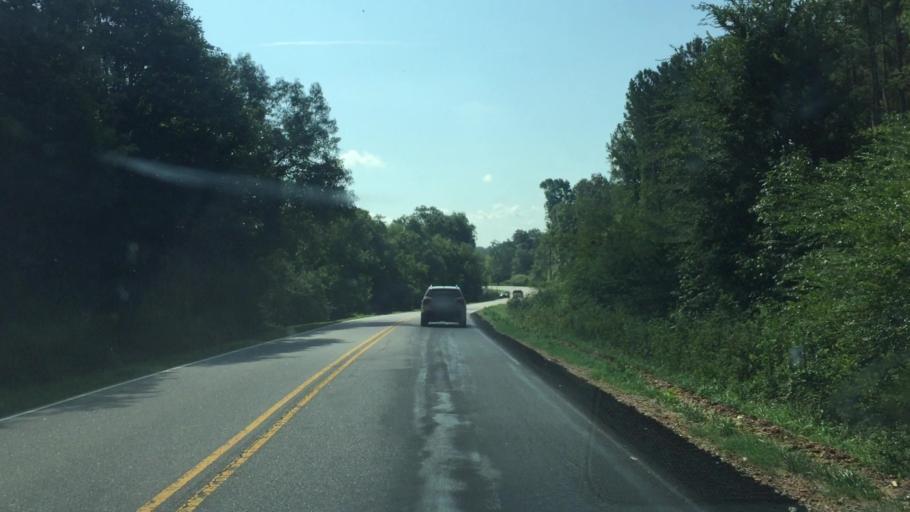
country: US
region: North Carolina
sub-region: Anson County
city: Burnsville
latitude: 35.1205
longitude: -80.3480
